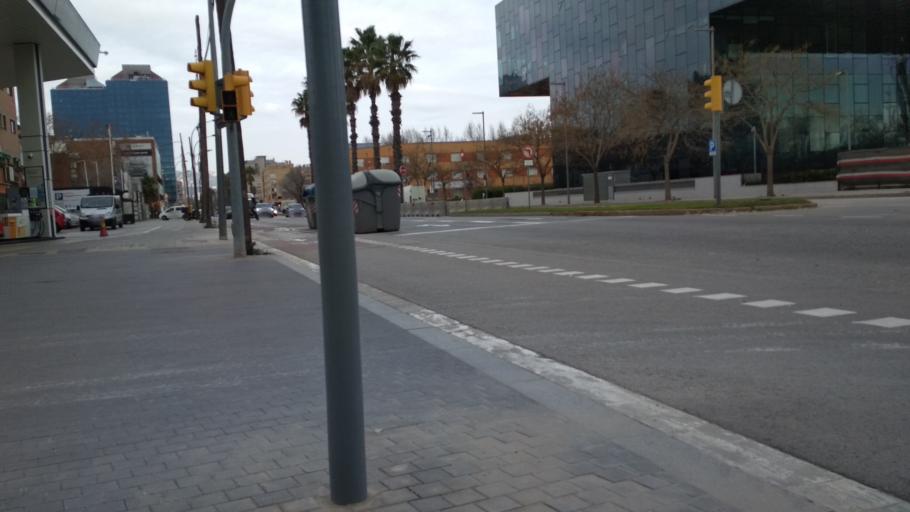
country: ES
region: Catalonia
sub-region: Provincia de Barcelona
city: Sants-Montjuic
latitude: 41.3529
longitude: 2.1442
